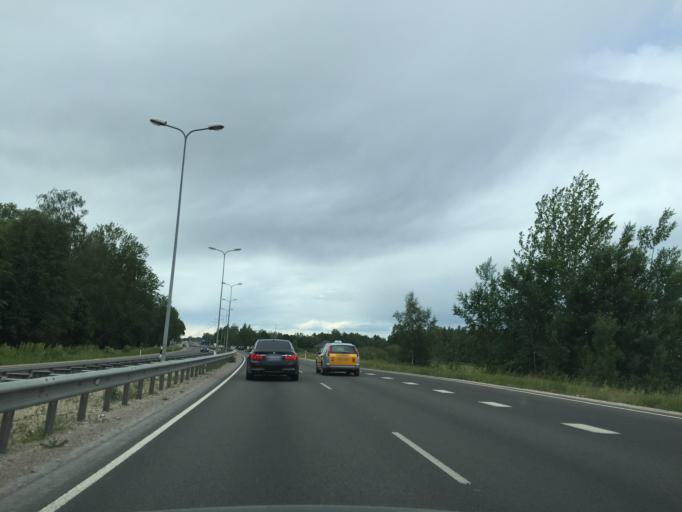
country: LV
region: Marupe
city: Marupe
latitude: 56.9237
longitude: 23.9982
